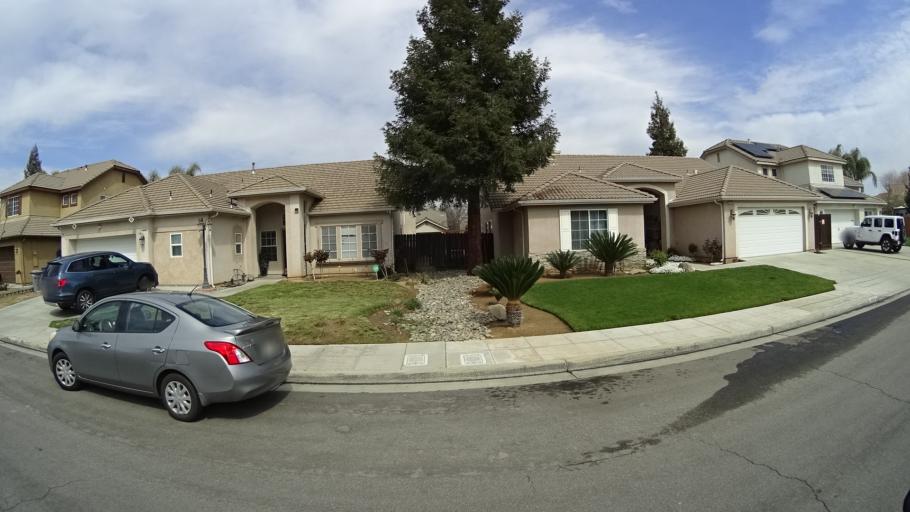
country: US
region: California
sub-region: Fresno County
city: West Park
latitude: 36.8193
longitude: -119.8860
